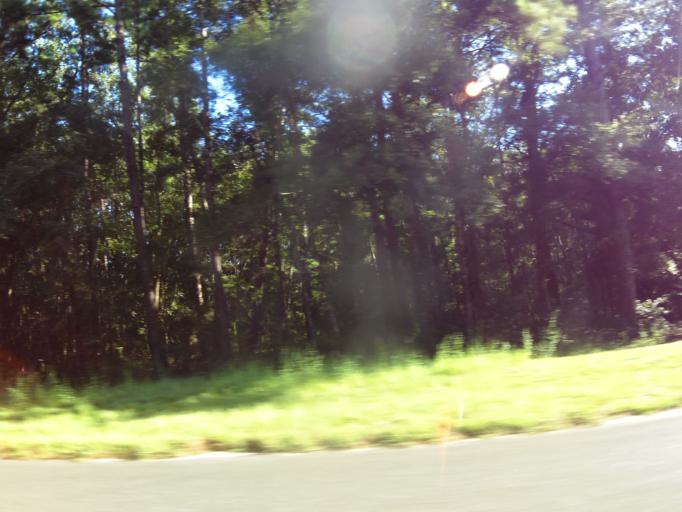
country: US
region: Florida
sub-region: Wakulla County
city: Crawfordville
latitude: 30.0634
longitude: -84.5040
